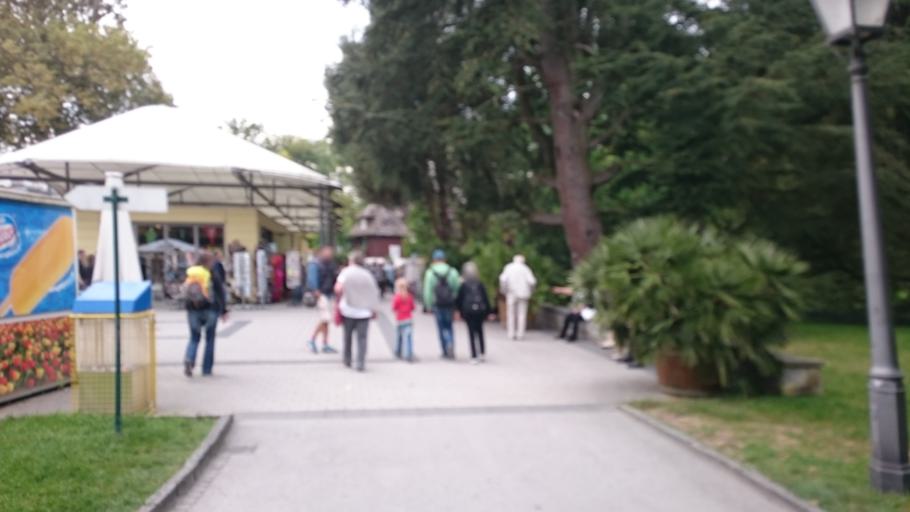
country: DE
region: Baden-Wuerttemberg
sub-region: Freiburg Region
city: Konstanz
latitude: 47.7044
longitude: 9.1908
